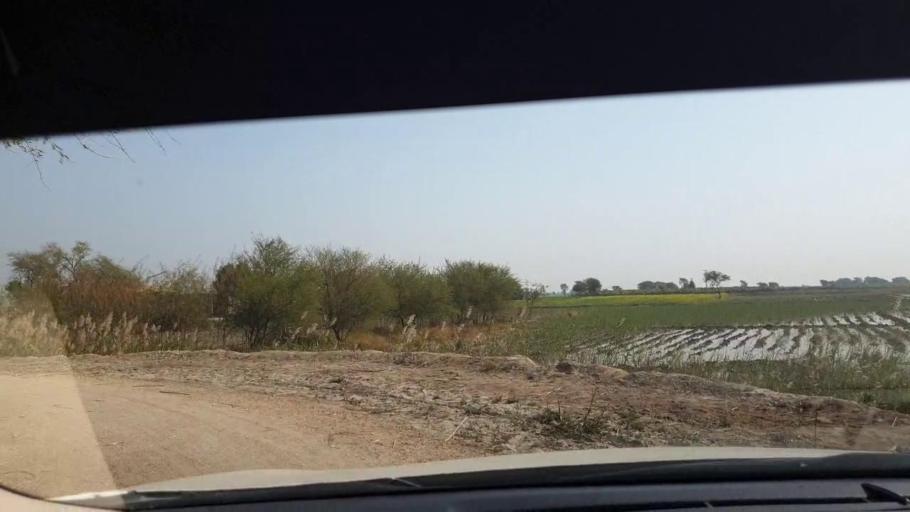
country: PK
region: Sindh
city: Tando Adam
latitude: 25.7275
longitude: 68.7083
